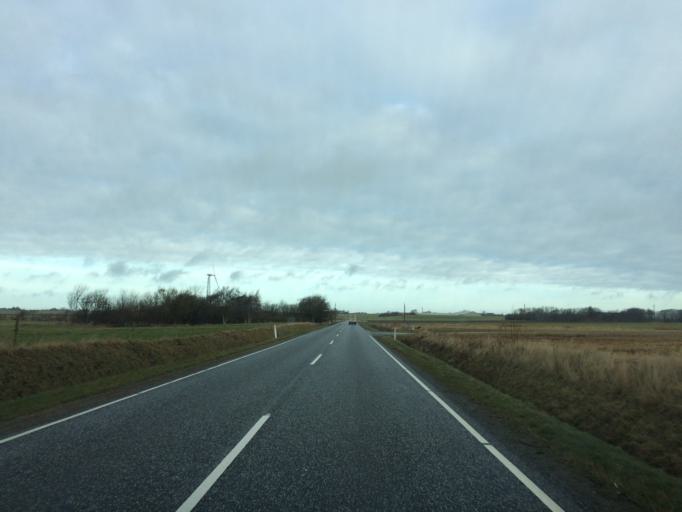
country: DK
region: Central Jutland
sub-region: Struer Kommune
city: Struer
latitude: 56.4470
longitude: 8.5350
